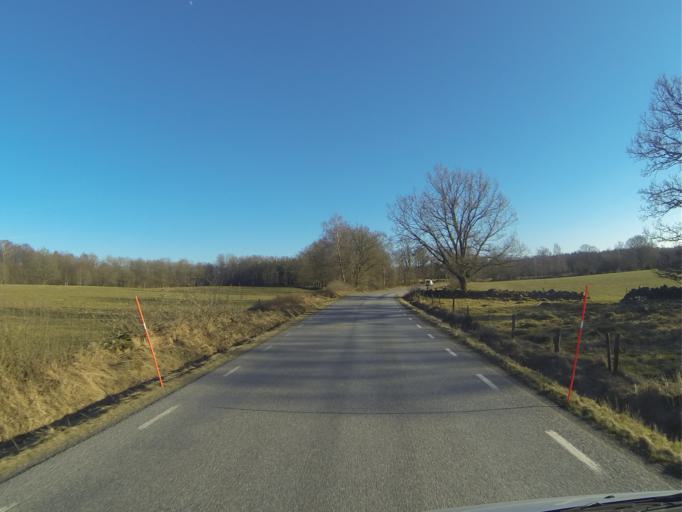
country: SE
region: Skane
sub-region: Horby Kommun
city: Hoerby
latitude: 55.8935
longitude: 13.6657
